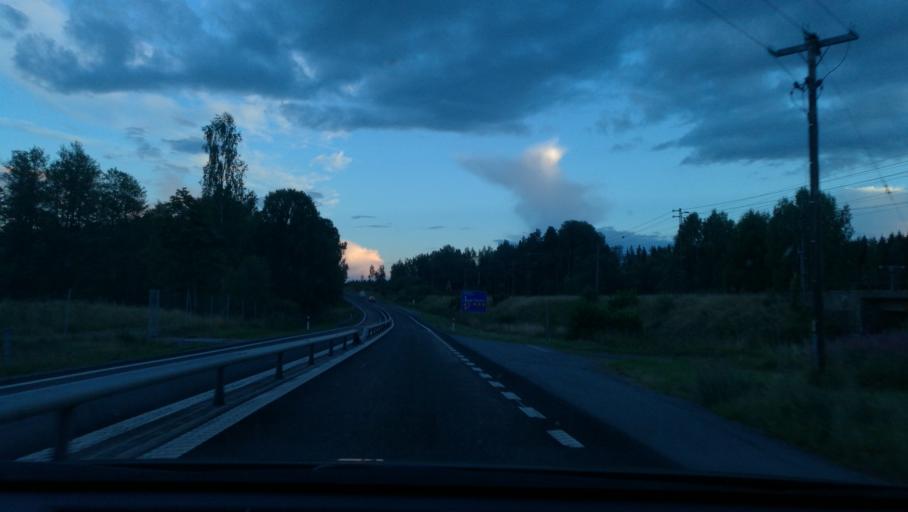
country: SE
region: Soedermanland
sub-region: Katrineholms Kommun
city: Katrineholm
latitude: 58.8714
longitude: 16.1967
